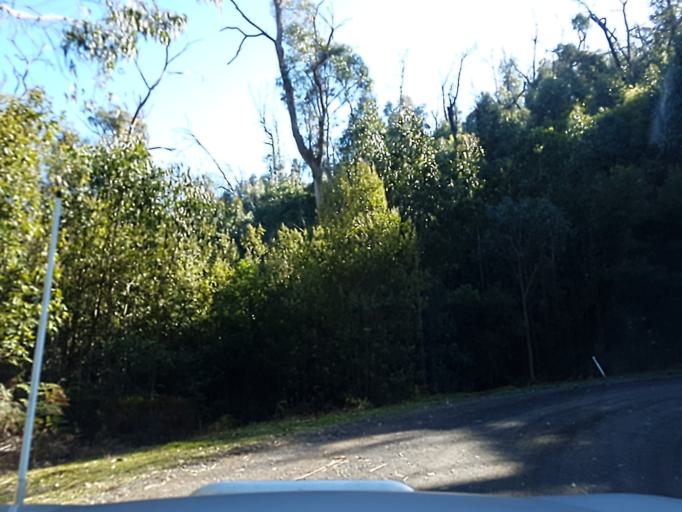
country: AU
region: Victoria
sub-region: Yarra Ranges
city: Yarra Glen
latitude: -37.5589
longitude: 145.3731
